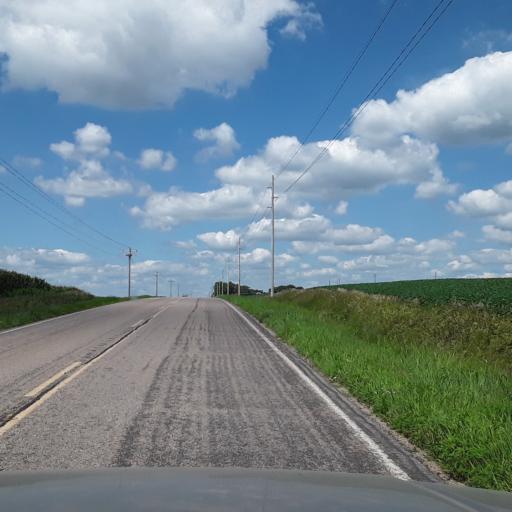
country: US
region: Nebraska
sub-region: Nance County
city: Genoa
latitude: 41.5508
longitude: -97.6961
